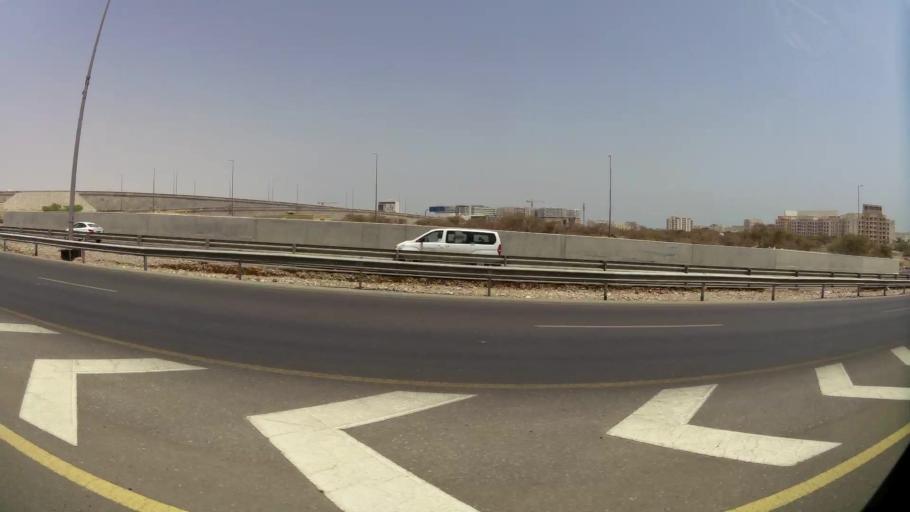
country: OM
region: Muhafazat Masqat
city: Bawshar
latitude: 23.5822
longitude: 58.4191
